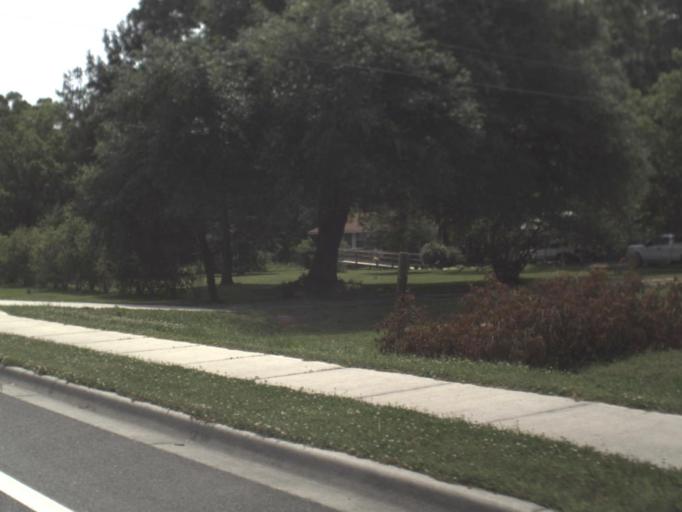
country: US
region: Florida
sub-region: Nassau County
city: Callahan
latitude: 30.5817
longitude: -81.8105
